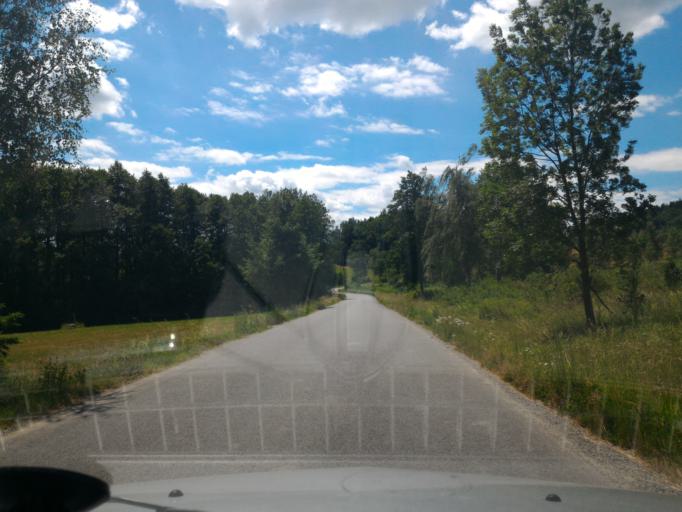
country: CZ
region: Vysocina
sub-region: Okres Jihlava
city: Telc
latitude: 49.2184
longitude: 15.3938
